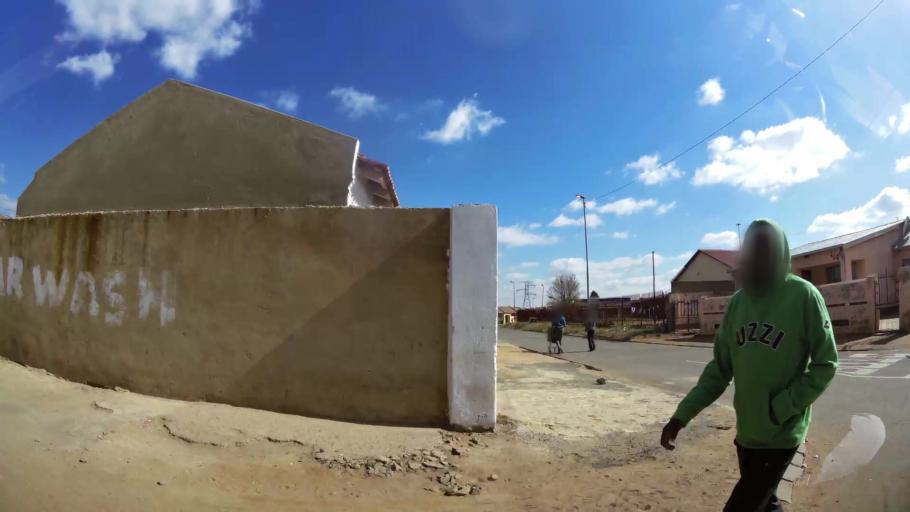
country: ZA
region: Gauteng
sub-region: West Rand District Municipality
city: Krugersdorp
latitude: -26.1421
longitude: 27.7963
